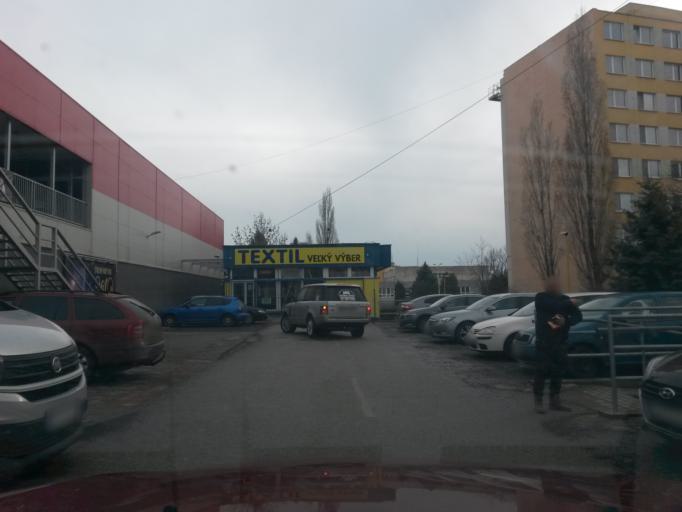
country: SK
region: Kosicky
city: Kosice
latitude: 48.7293
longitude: 21.2882
